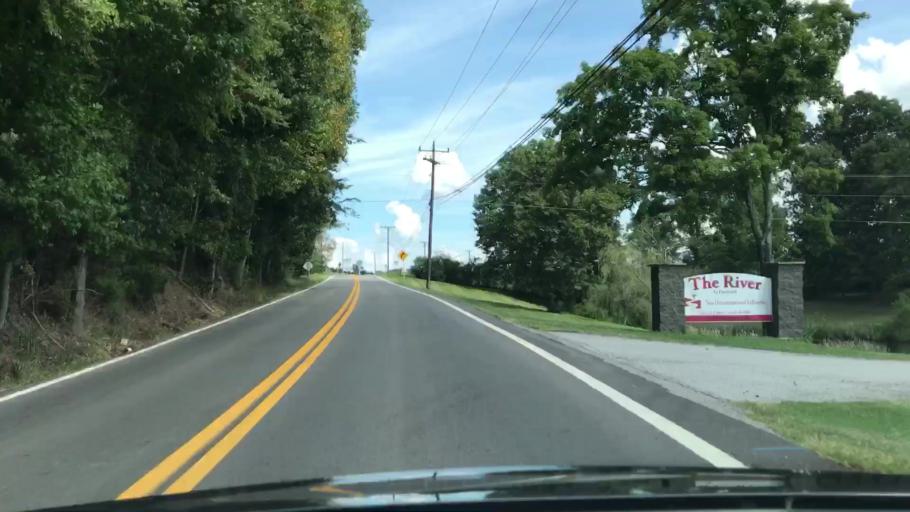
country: US
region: Tennessee
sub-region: Sumner County
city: Portland
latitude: 36.5324
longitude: -86.5373
